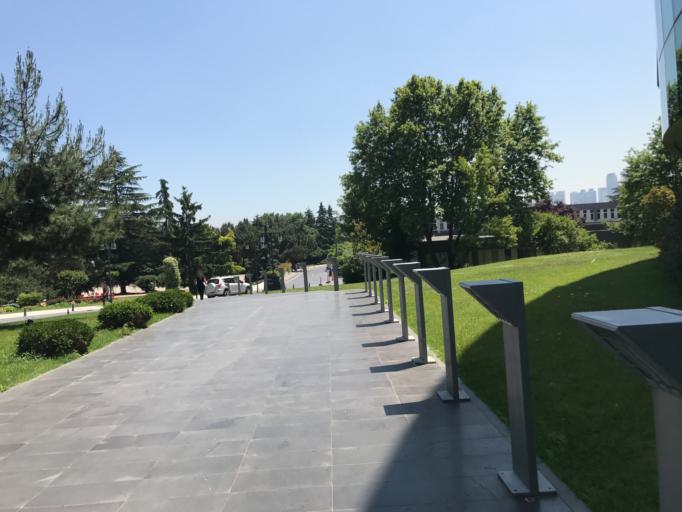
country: TR
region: Istanbul
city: Sisli
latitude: 41.1074
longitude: 29.0215
